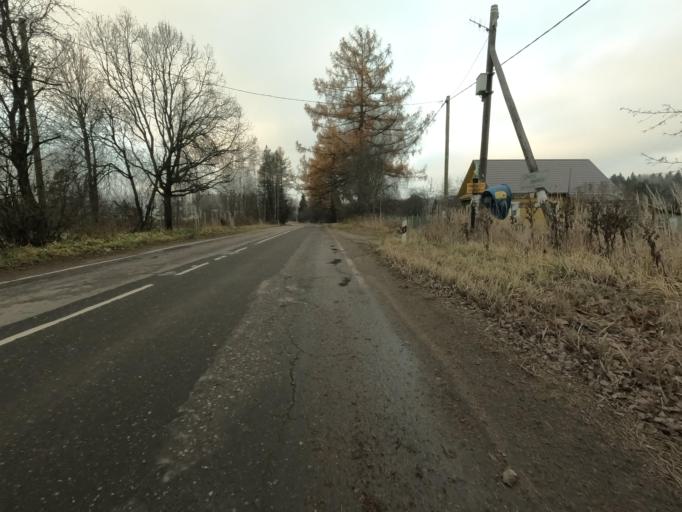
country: RU
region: Leningrad
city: Kirovsk
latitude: 59.8018
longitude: 30.9904
